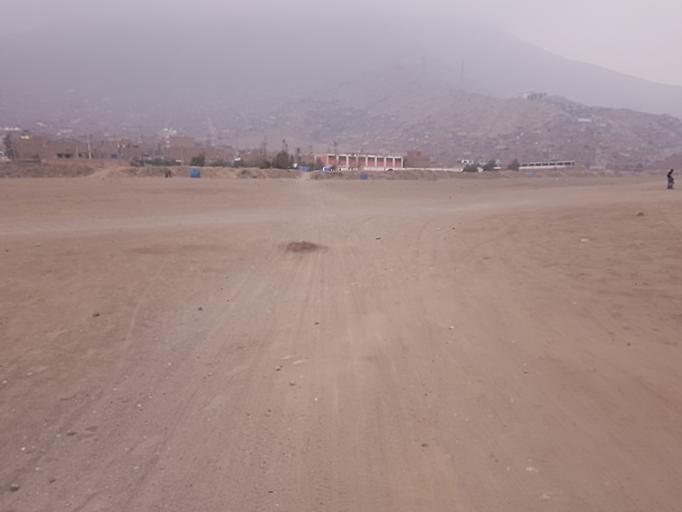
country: PE
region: Lima
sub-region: Lima
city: Santa Maria
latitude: -11.9834
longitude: -76.9154
